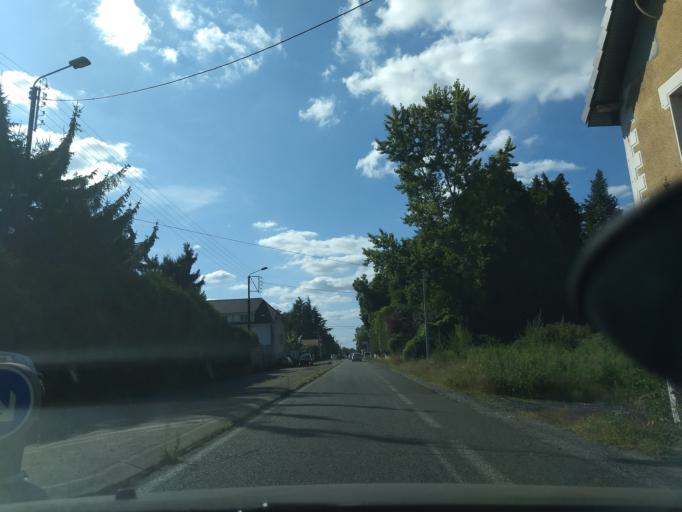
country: FR
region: Aquitaine
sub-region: Departement des Pyrenees-Atlantiques
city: Idron
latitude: 43.3015
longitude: -0.3150
